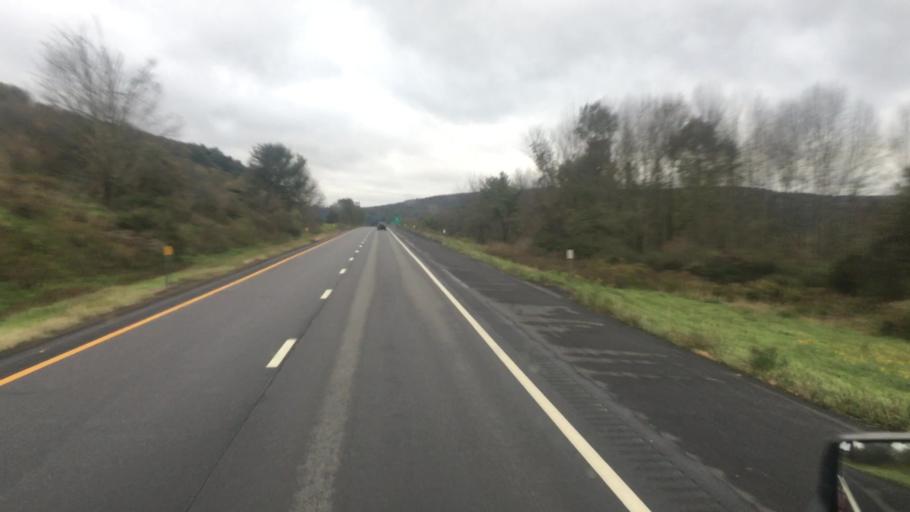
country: US
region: New York
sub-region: Chenango County
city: Bainbridge
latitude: 42.2915
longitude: -75.4460
